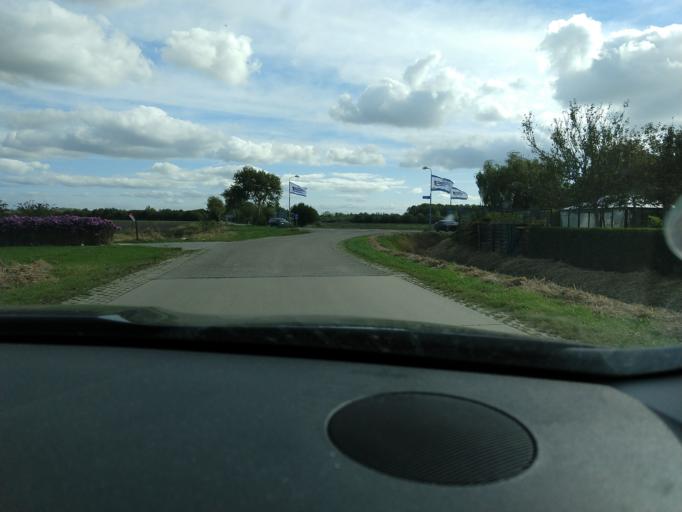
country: NL
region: Zeeland
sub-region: Gemeente Vlissingen
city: Vlissingen
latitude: 51.5012
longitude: 3.4991
